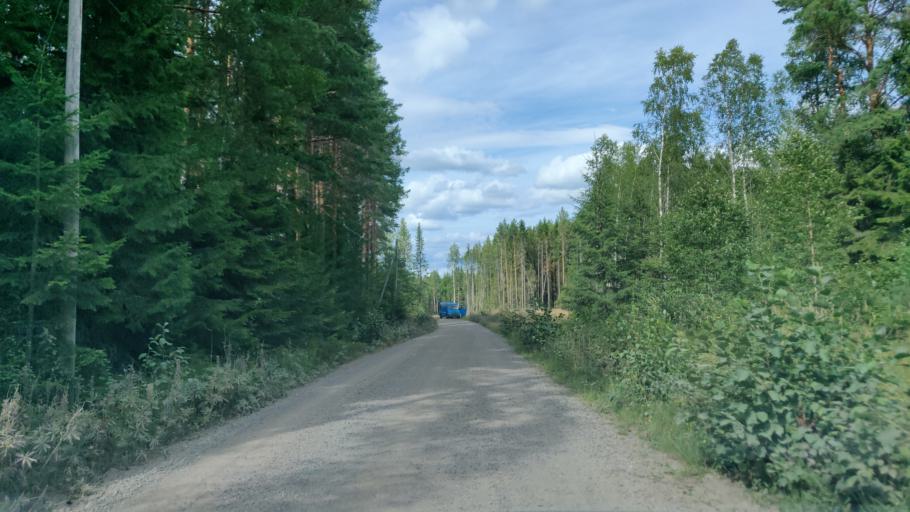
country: SE
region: Vaermland
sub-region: Hagfors Kommun
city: Hagfors
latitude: 60.0112
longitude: 13.7070
